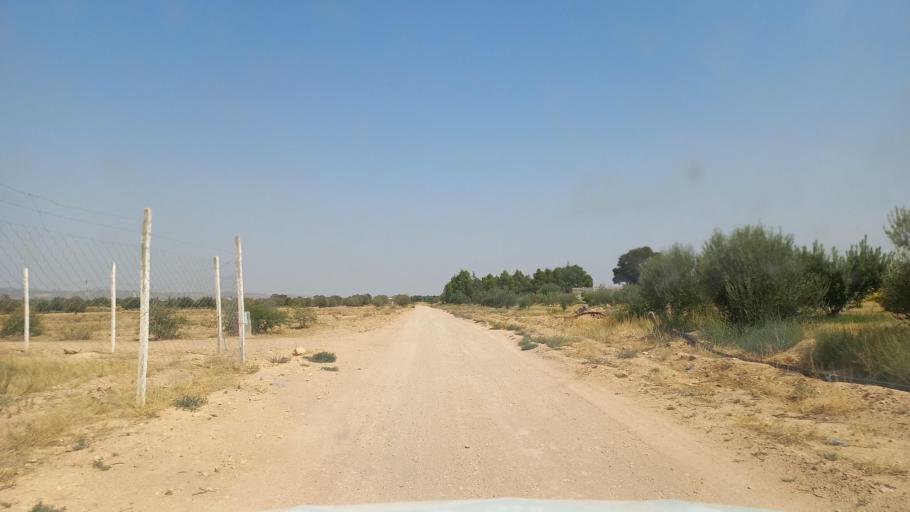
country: TN
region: Al Qasrayn
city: Kasserine
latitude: 35.2490
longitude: 9.0144
